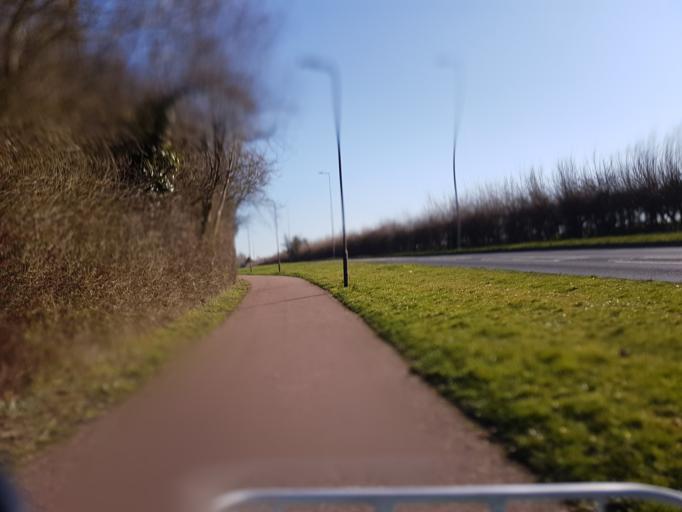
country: GB
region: England
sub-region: Buckinghamshire
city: Newton Longville
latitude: 51.9887
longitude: -0.7830
